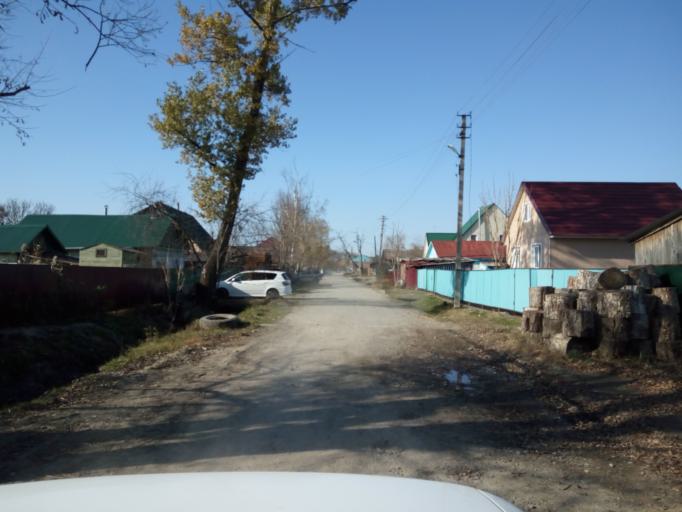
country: RU
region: Primorskiy
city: Dal'nerechensk
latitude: 45.9232
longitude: 133.7333
